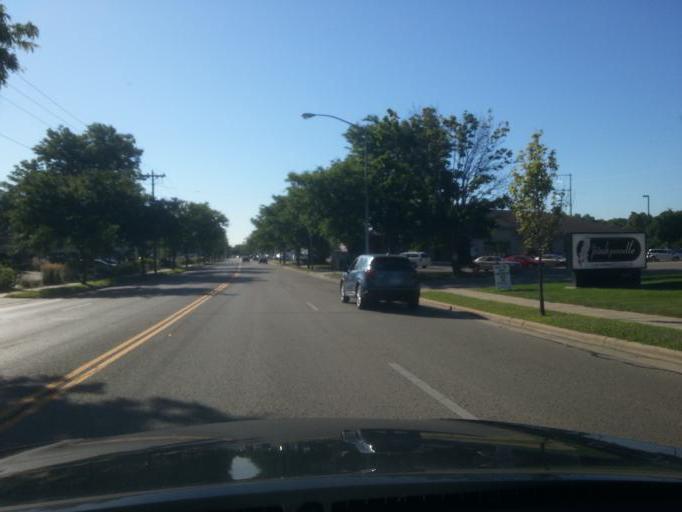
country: US
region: Wisconsin
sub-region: Dane County
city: Shorewood Hills
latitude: 43.0533
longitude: -89.4855
